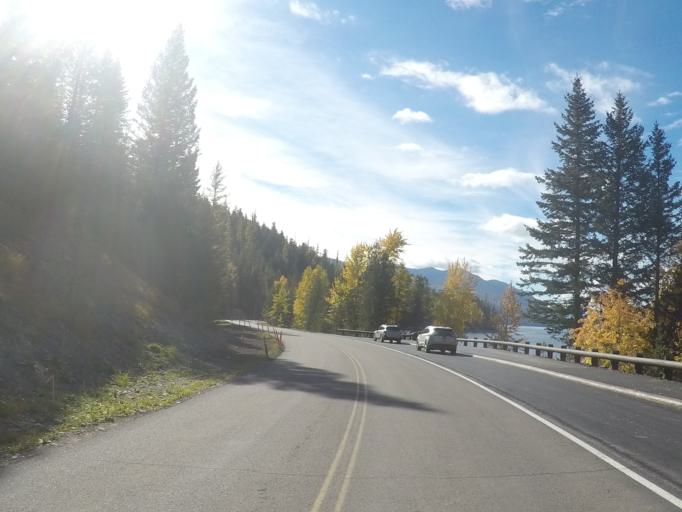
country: US
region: Montana
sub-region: Flathead County
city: Columbia Falls
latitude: 48.6117
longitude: -113.8814
